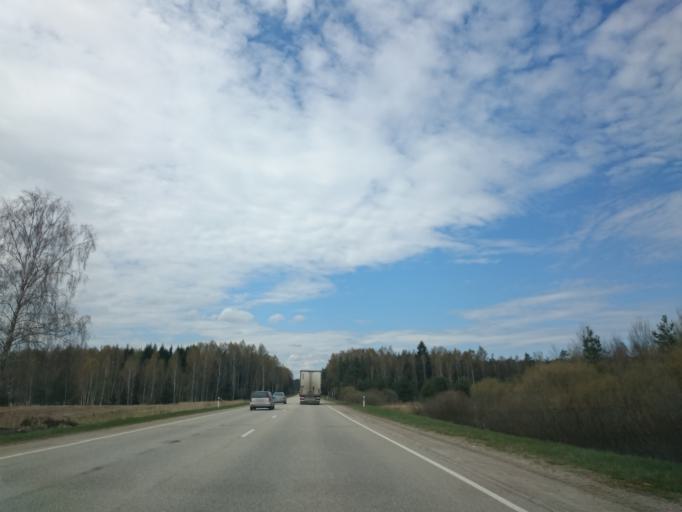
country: LV
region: Tukuma Rajons
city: Tukums
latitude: 56.9430
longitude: 23.1546
